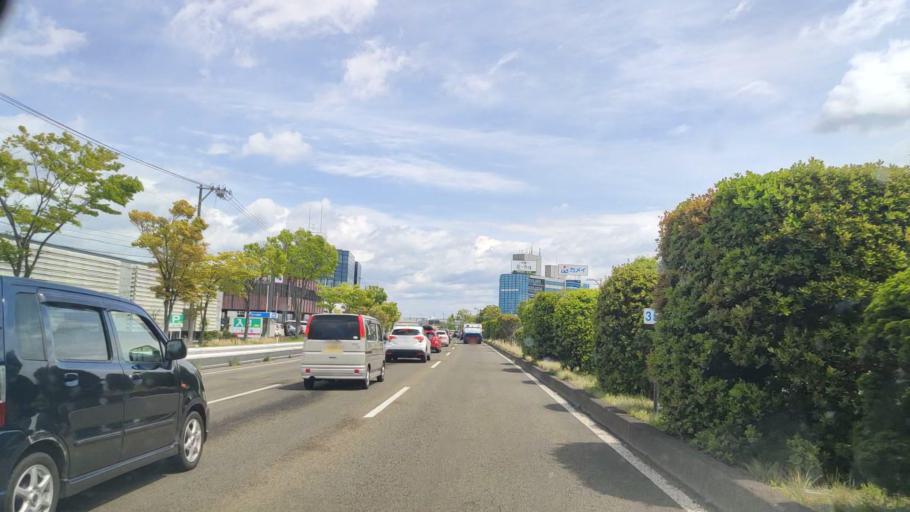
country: JP
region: Miyagi
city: Sendai-shi
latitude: 38.2545
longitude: 140.9330
